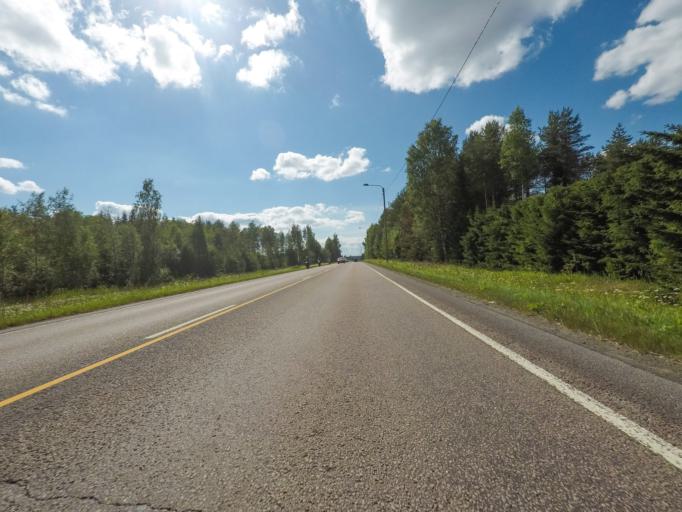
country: FI
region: Southern Savonia
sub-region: Savonlinna
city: Savonlinna
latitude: 61.8822
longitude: 29.0634
